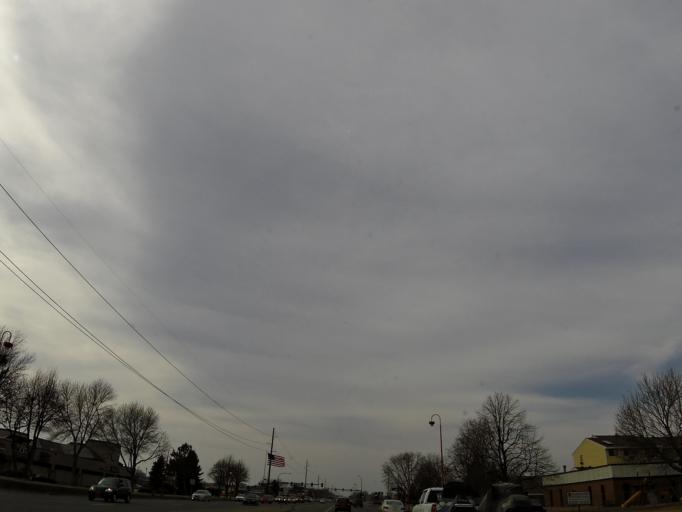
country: US
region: Minnesota
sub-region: Dakota County
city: Apple Valley
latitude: 44.7320
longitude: -93.2150
